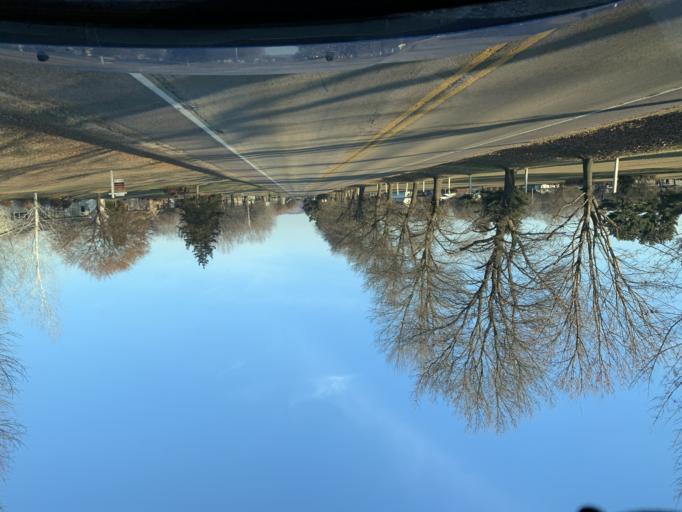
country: US
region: Wisconsin
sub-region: Sauk County
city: Spring Green
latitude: 43.1695
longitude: -90.0640
